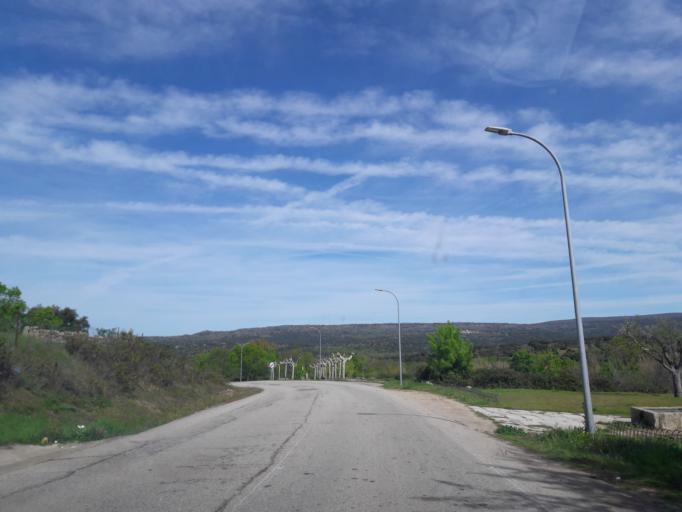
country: ES
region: Castille and Leon
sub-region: Provincia de Salamanca
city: Ledrada
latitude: 40.4711
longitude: -5.7213
